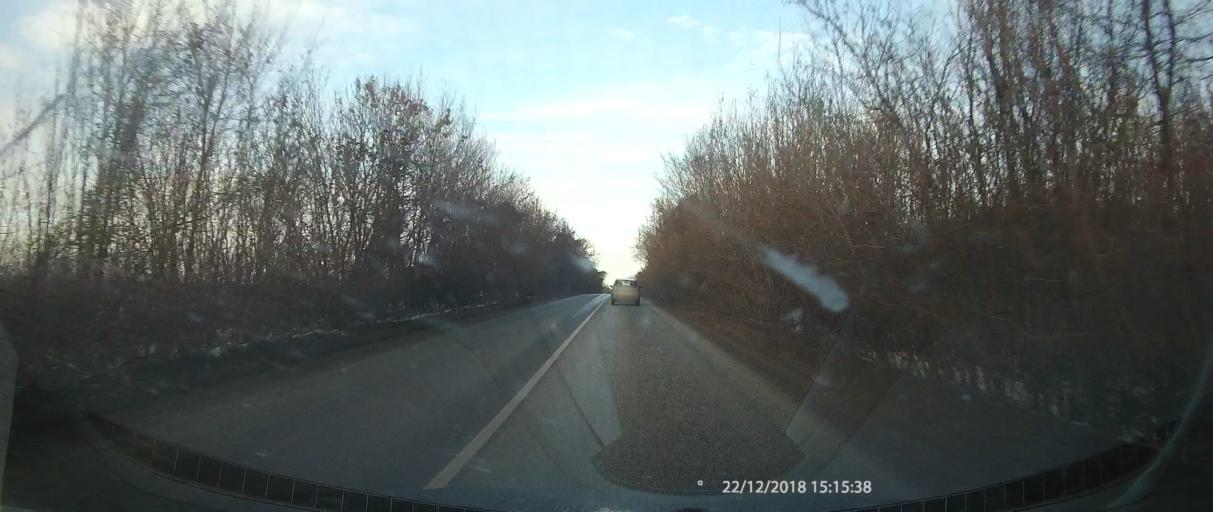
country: BG
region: Ruse
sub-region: Obshtina Dve Mogili
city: Dve Mogili
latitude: 43.5942
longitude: 25.8383
